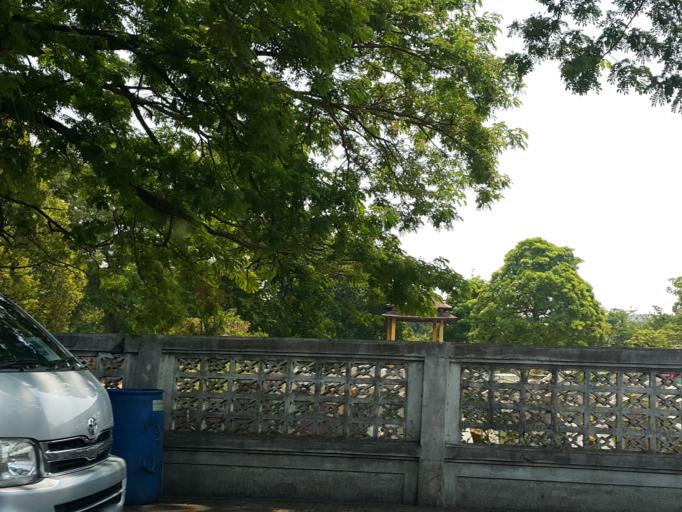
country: TH
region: Kanchanaburi
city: Kanchanaburi
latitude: 14.0299
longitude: 99.5259
